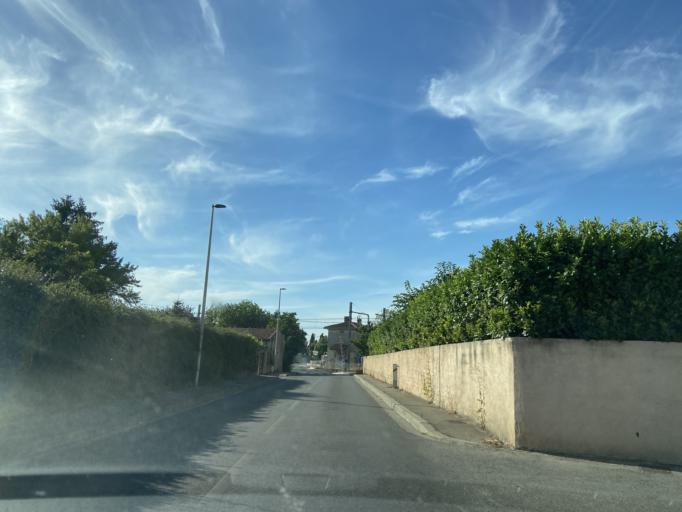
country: FR
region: Provence-Alpes-Cote d'Azur
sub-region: Departement des Bouches-du-Rhone
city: Miramas
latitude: 43.5806
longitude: 5.0075
